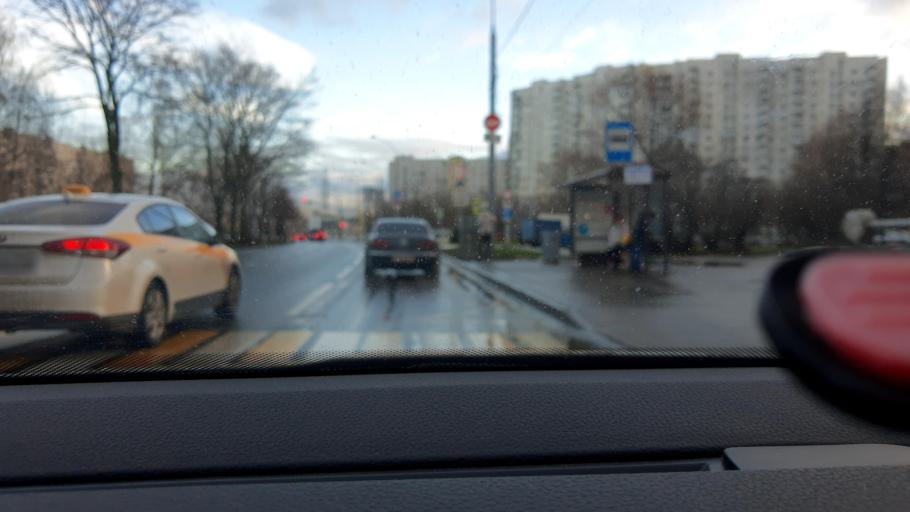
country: RU
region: Moscow
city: Bibirevo
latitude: 55.8917
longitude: 37.6194
